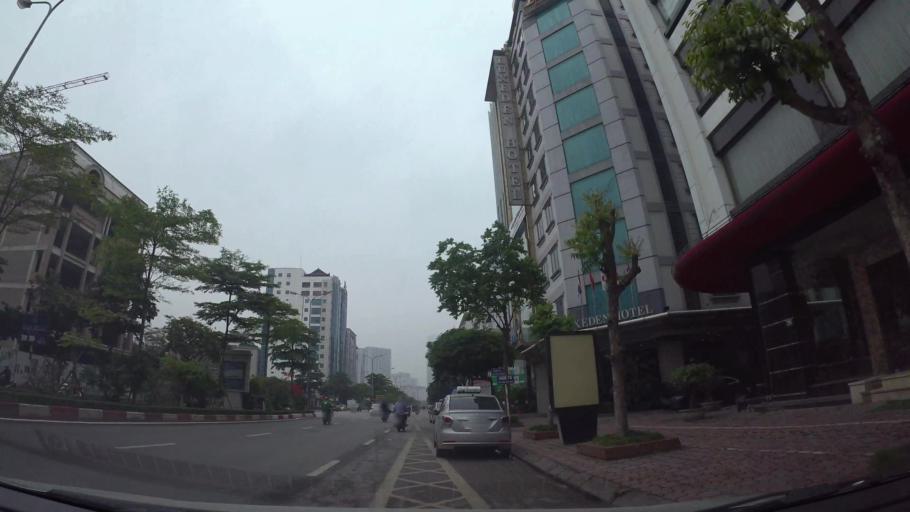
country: VN
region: Ha Noi
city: Cau Giay
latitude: 21.0337
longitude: 105.7888
